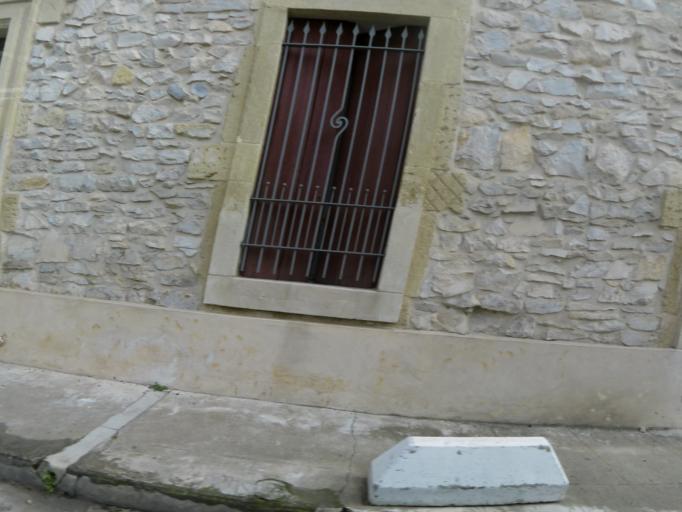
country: FR
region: Languedoc-Roussillon
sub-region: Departement du Gard
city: Calvisson
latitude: 43.7868
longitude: 4.1940
